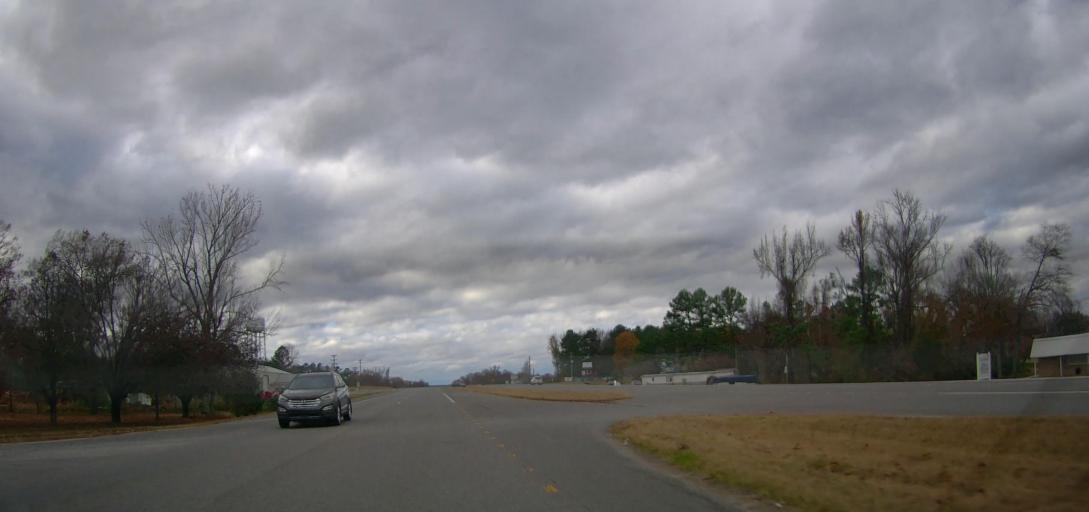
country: US
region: Alabama
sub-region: Lawrence County
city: Town Creek
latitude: 34.5909
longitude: -87.4277
